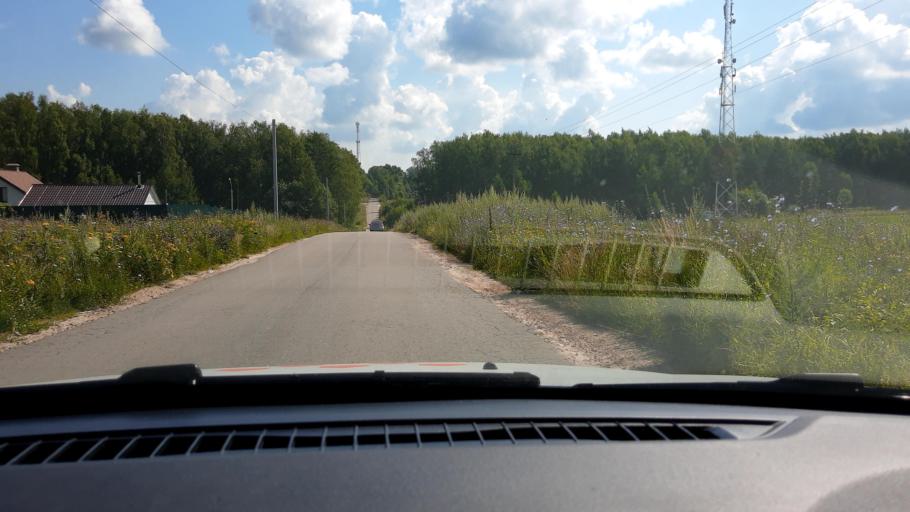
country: RU
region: Nizjnij Novgorod
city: Burevestnik
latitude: 56.0515
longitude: 43.9584
